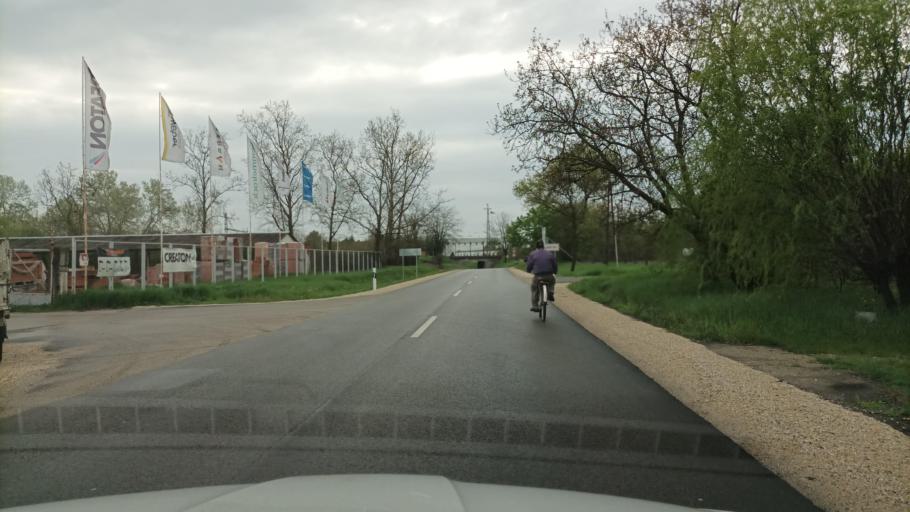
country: HU
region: Pest
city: Nagykoros
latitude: 47.0362
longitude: 19.7562
